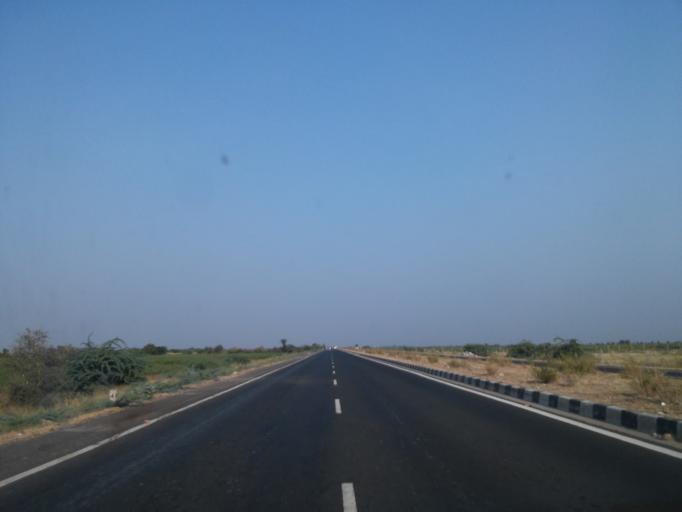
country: IN
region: Gujarat
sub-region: Surendranagar
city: Dhrangadhra
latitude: 23.0327
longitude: 71.6626
